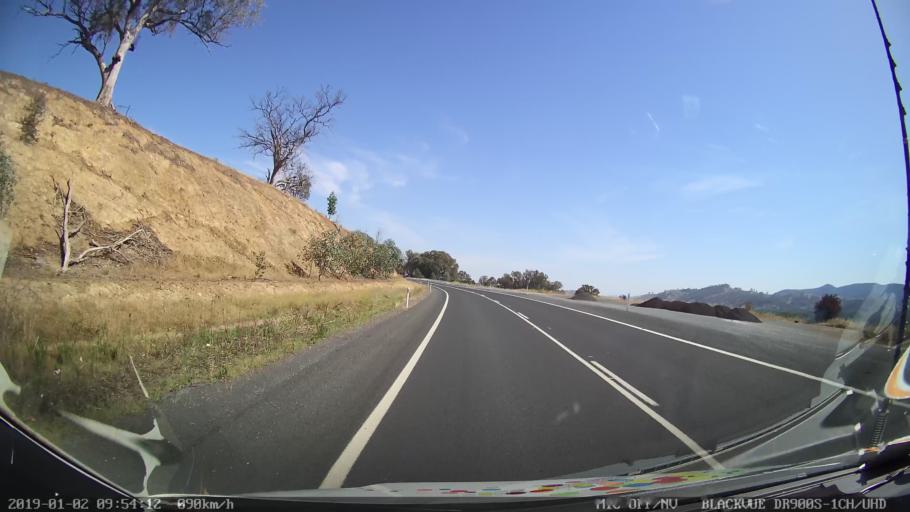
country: AU
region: New South Wales
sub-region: Tumut Shire
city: Tumut
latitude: -35.2385
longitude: 148.1977
